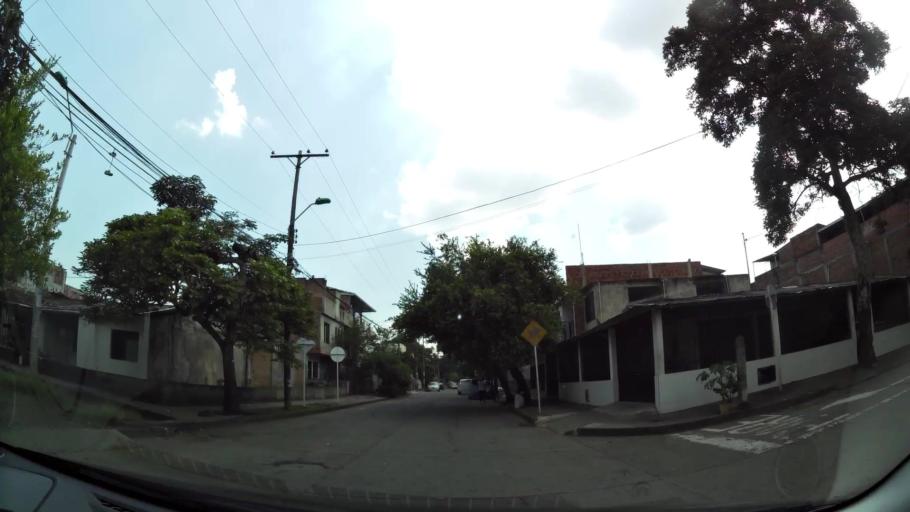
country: CO
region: Valle del Cauca
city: Cali
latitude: 3.4103
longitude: -76.5202
